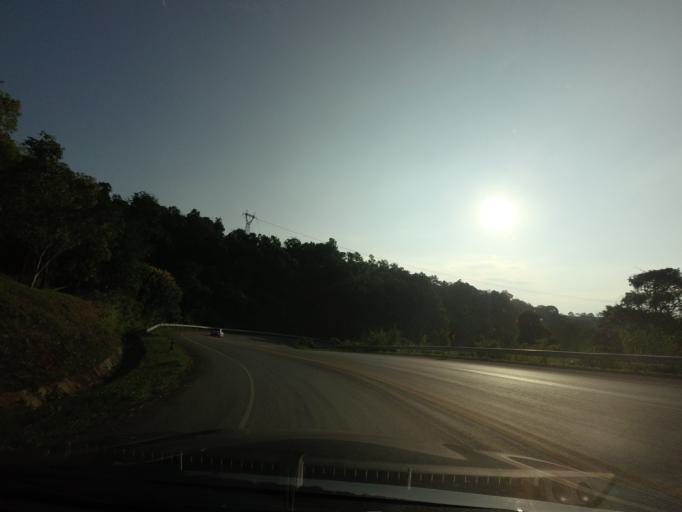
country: TH
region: Loei
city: Dan Sai
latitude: 17.2280
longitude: 101.1519
